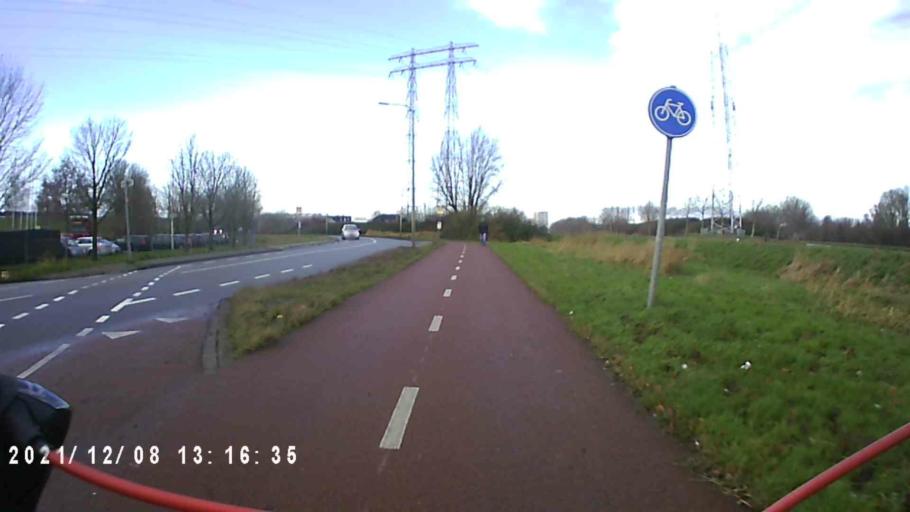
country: NL
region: Groningen
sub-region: Gemeente Haren
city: Haren
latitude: 53.1971
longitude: 6.6196
